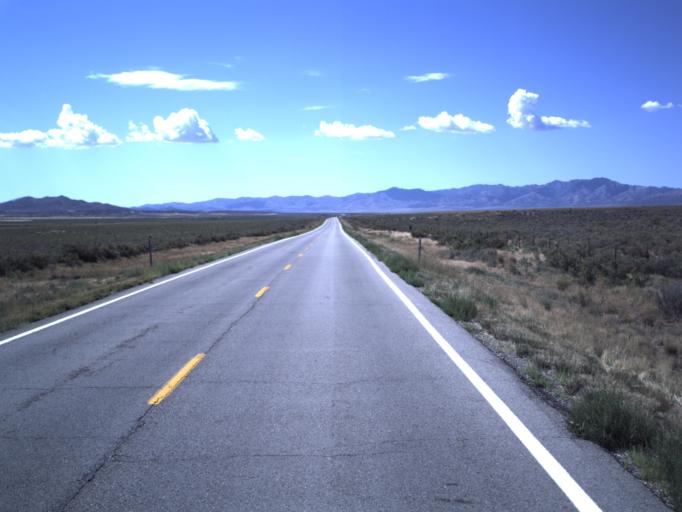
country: US
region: Utah
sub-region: Tooele County
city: Tooele
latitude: 40.2260
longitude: -112.4043
